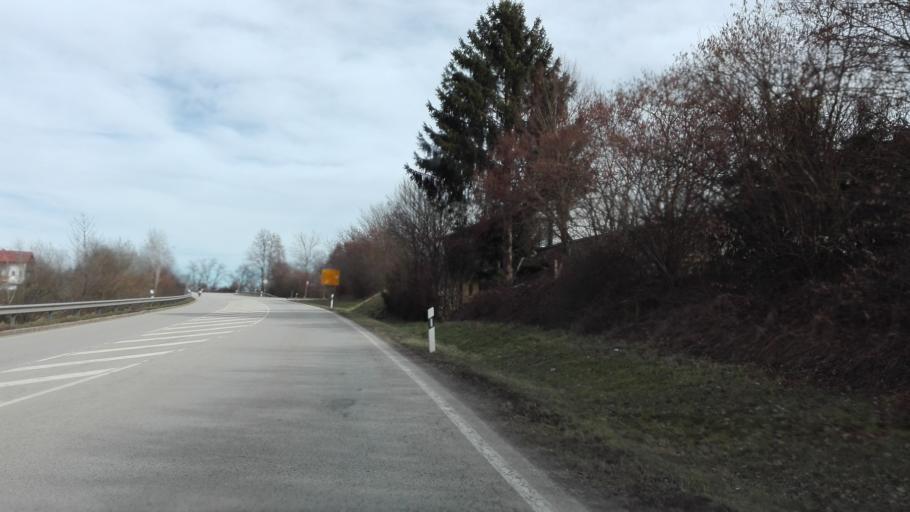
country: DE
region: Bavaria
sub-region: Lower Bavaria
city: Thyrnau
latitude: 48.5984
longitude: 13.5286
